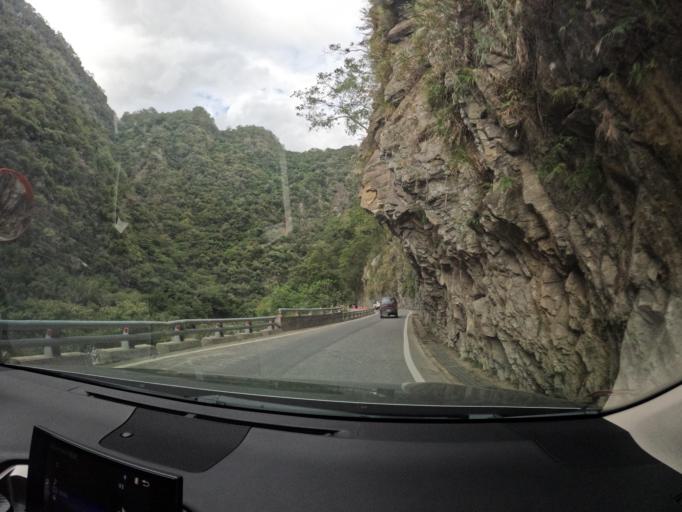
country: TW
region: Taiwan
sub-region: Taitung
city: Taitung
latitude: 23.1386
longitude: 121.1089
